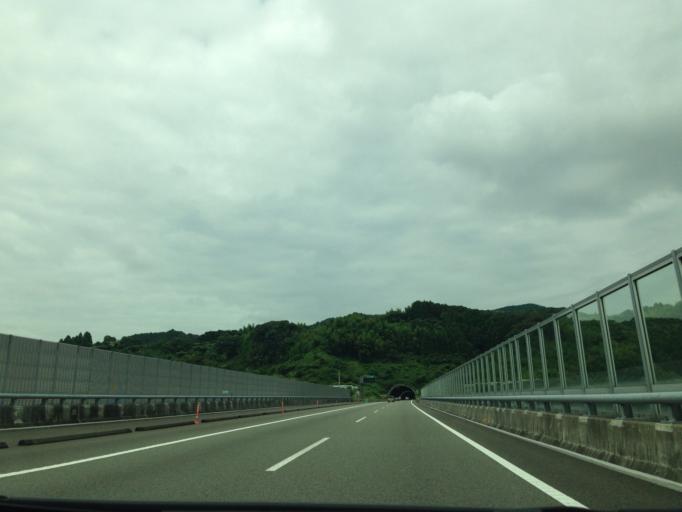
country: JP
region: Shizuoka
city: Fujieda
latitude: 34.8861
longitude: 138.2147
